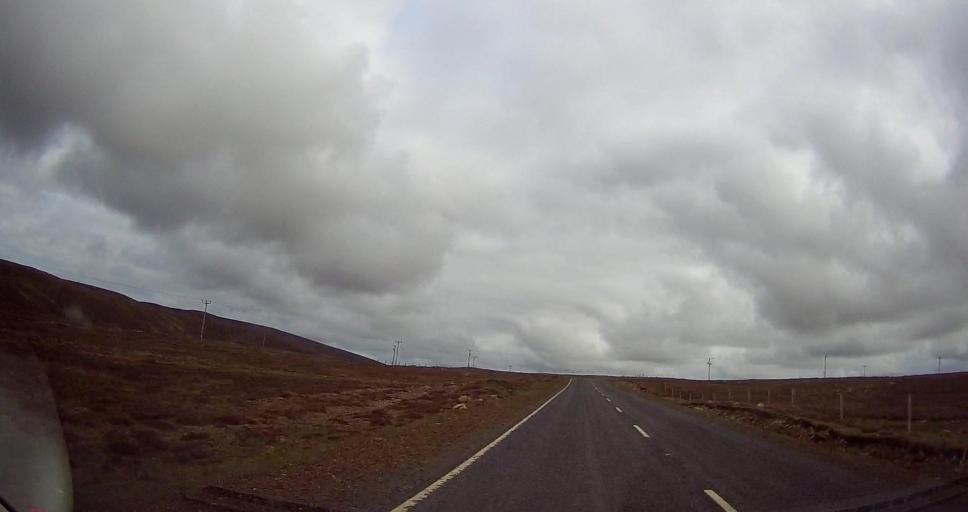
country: GB
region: Scotland
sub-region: Shetland Islands
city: Shetland
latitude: 60.7177
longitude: -0.9127
